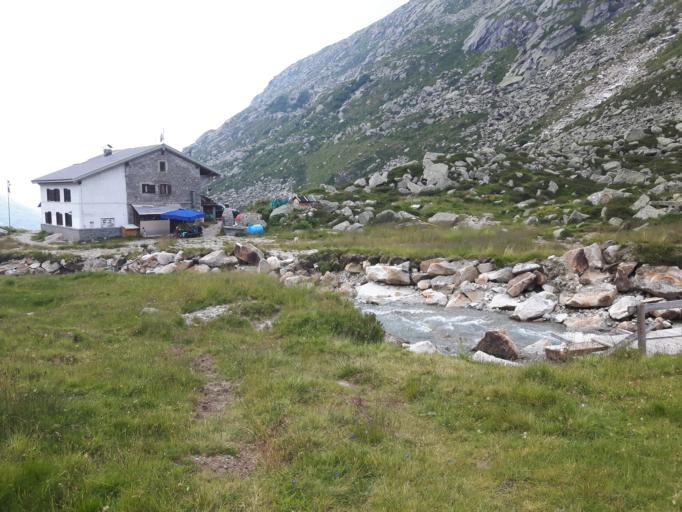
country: IT
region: Lombardy
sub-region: Provincia di Brescia
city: Saviore
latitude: 46.1239
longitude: 10.5025
